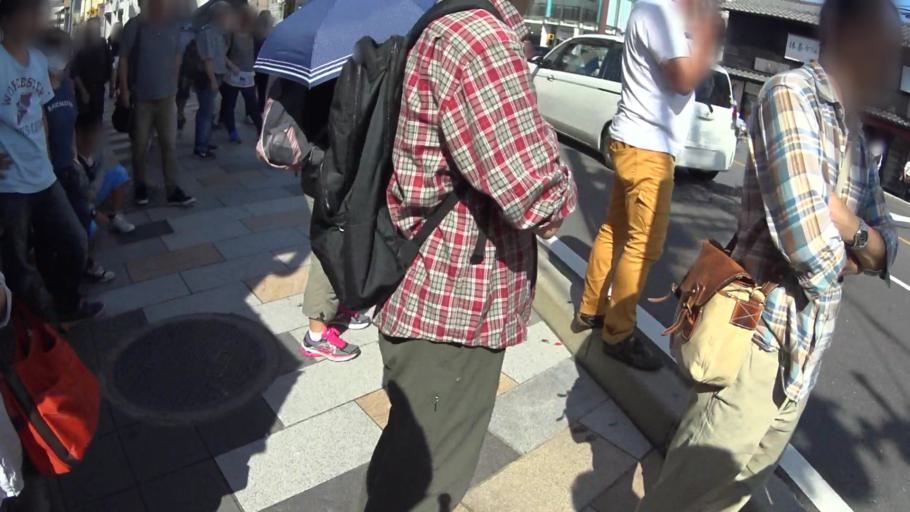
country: JP
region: Kyoto
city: Kyoto
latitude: 34.9949
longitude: 135.7762
